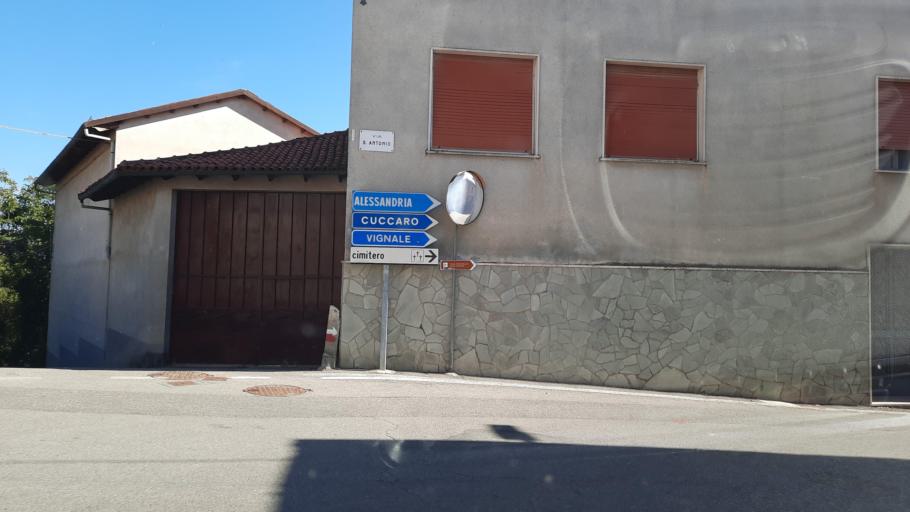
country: IT
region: Piedmont
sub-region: Provincia di Alessandria
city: Camagna Monferrato
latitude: 45.0170
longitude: 8.4291
